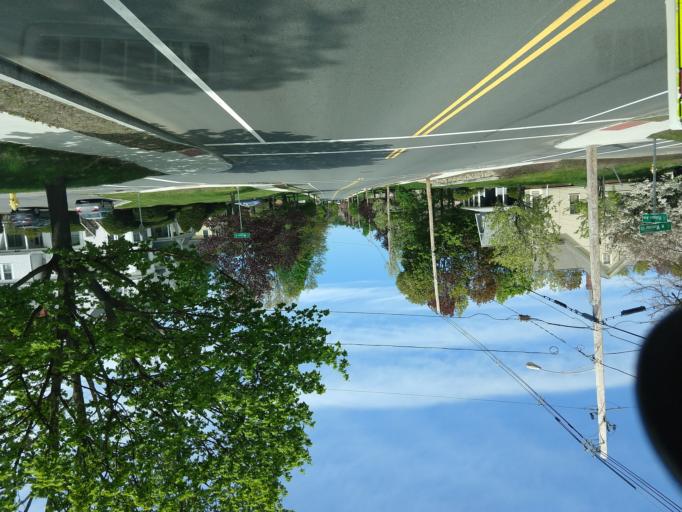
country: US
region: Massachusetts
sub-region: Essex County
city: Amesbury
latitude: 42.8469
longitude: -70.9370
